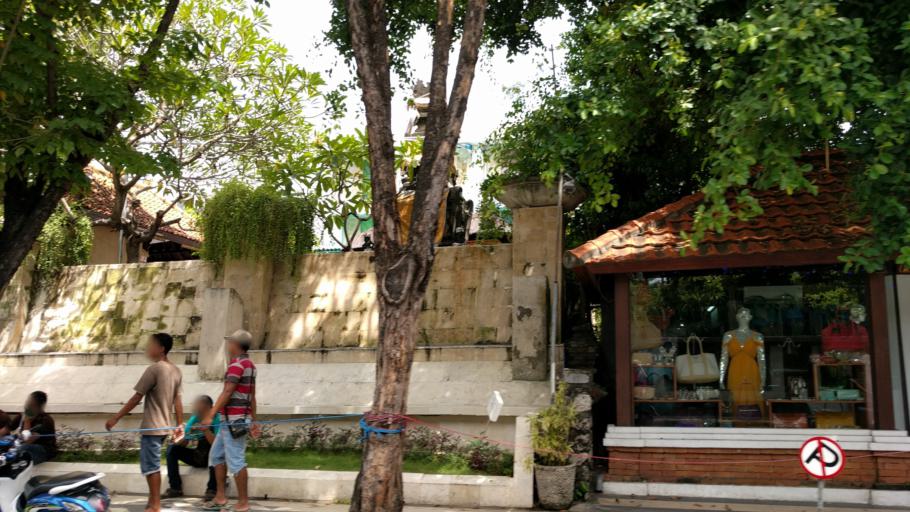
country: ID
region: Bali
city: Jabajero
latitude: -8.7283
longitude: 115.1691
